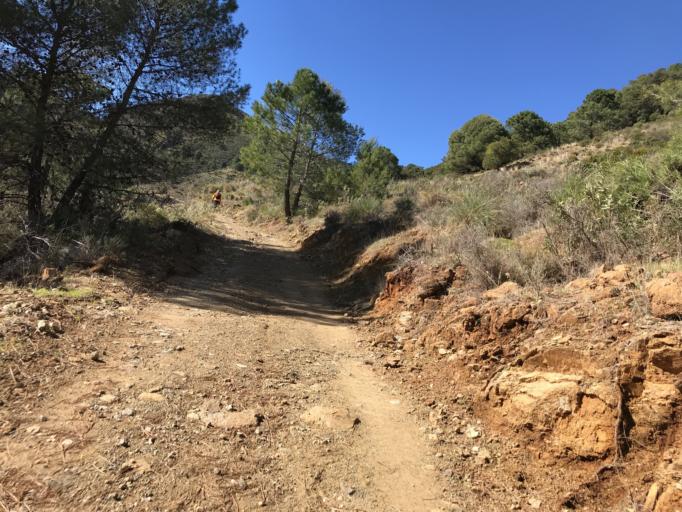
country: ES
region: Andalusia
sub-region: Provincia de Malaga
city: Tolox
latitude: 36.6736
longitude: -4.9161
